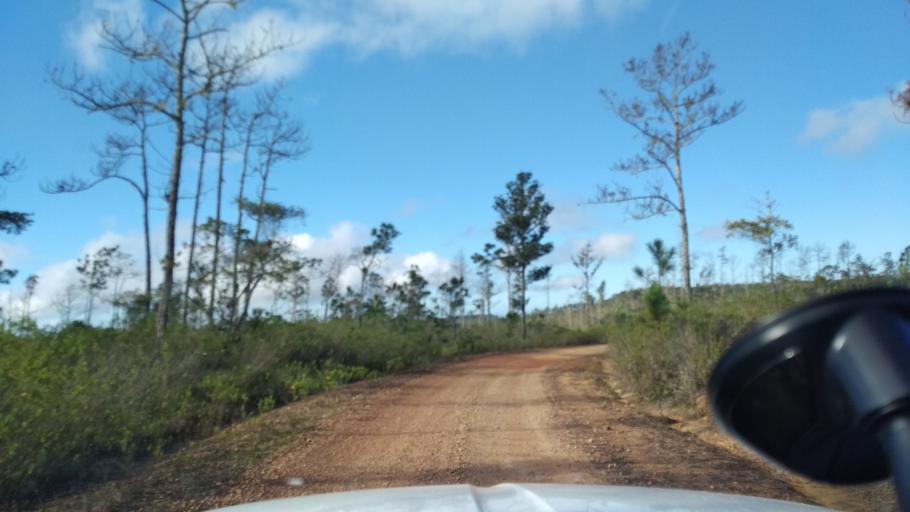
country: BZ
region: Cayo
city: Belmopan
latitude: 16.9955
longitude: -88.8356
